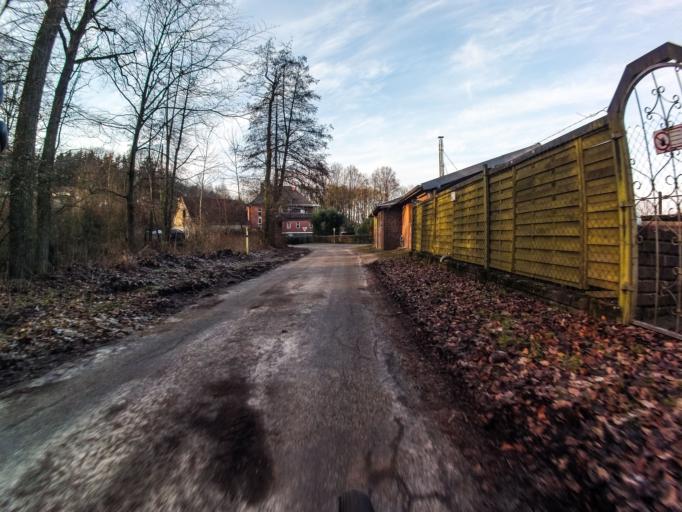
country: DE
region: North Rhine-Westphalia
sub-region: Regierungsbezirk Munster
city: Mettingen
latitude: 52.2882
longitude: 7.7972
